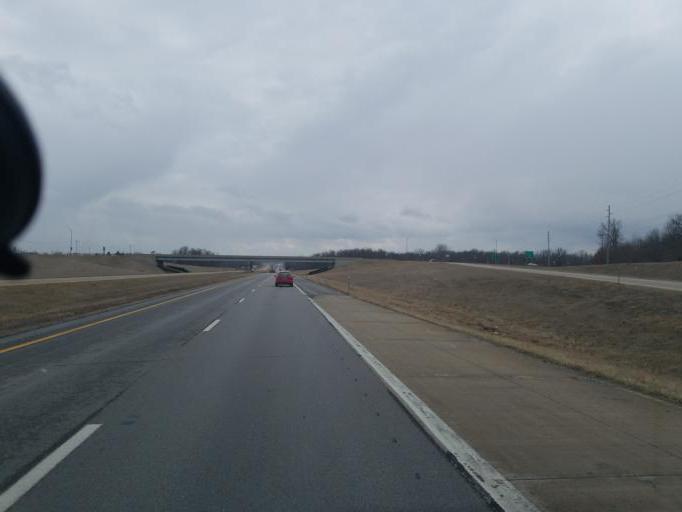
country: US
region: Missouri
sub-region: Randolph County
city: Moberly
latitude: 39.3963
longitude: -92.4131
